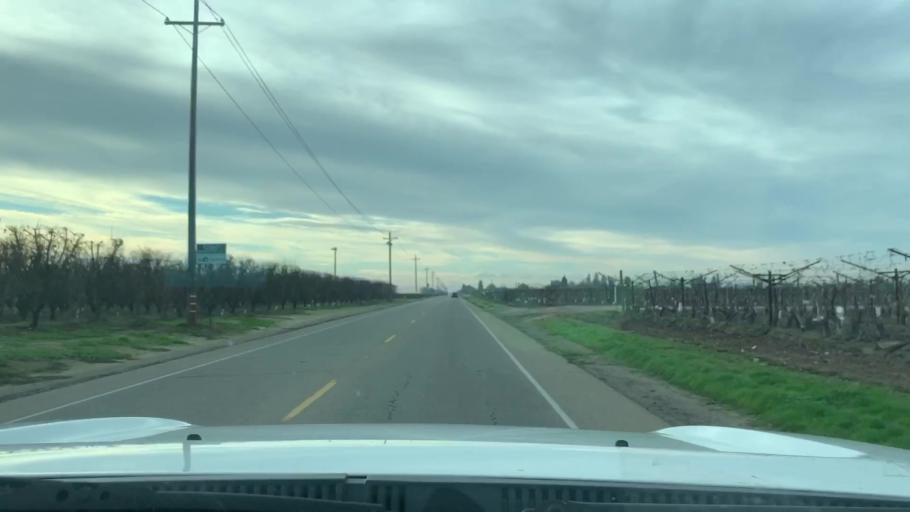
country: US
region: California
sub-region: Fresno County
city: Fowler
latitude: 36.6054
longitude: -119.6696
